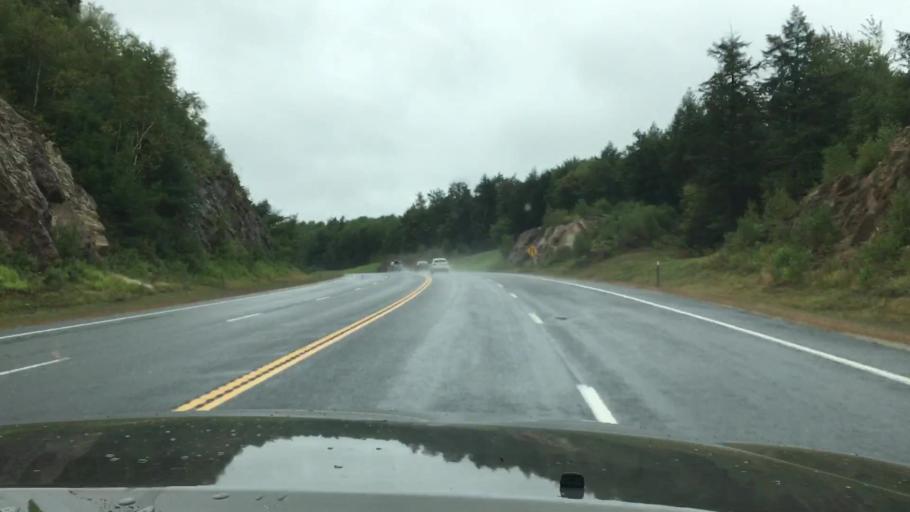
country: US
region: New Hampshire
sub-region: Cheshire County
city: Harrisville
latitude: 43.0071
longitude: -72.1634
